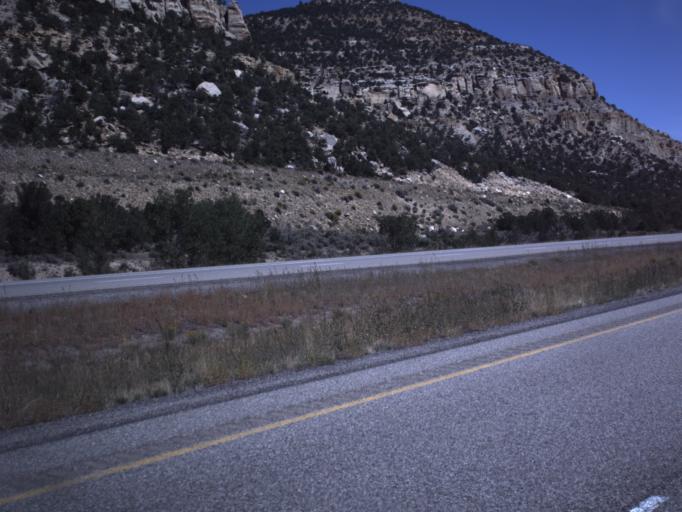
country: US
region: Utah
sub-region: Wayne County
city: Loa
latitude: 38.7565
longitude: -111.4390
